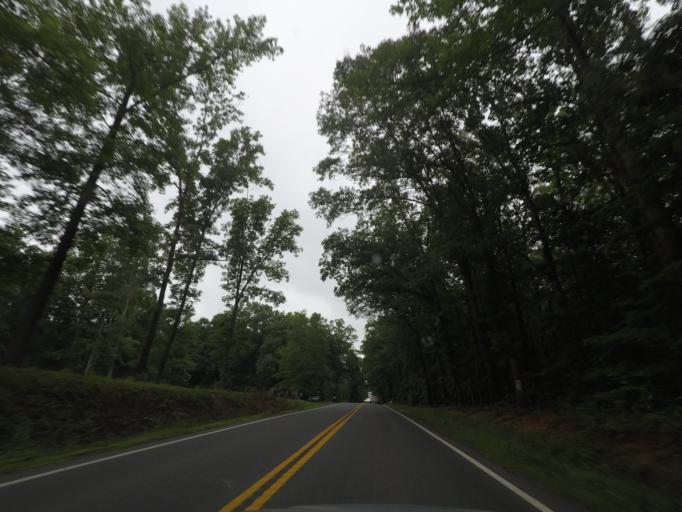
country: US
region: Virginia
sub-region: Orange County
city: Gordonsville
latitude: 38.0031
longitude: -78.1921
